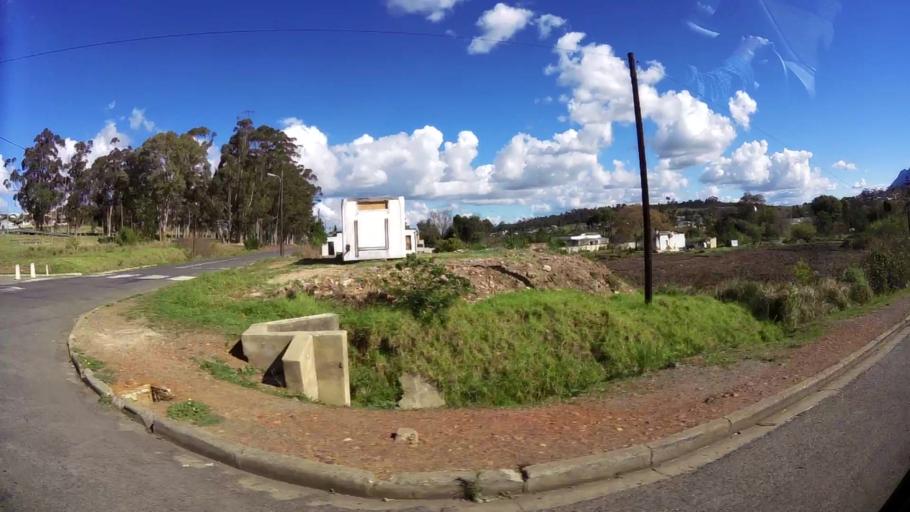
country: ZA
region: Western Cape
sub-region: Overberg District Municipality
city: Swellendam
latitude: -34.0296
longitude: 20.4413
